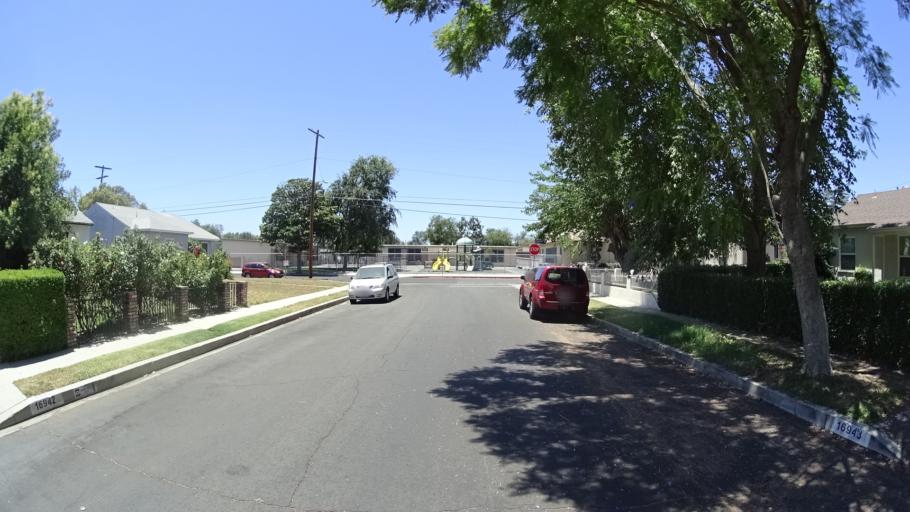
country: US
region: California
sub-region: Los Angeles County
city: Northridge
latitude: 34.1987
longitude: -118.5028
